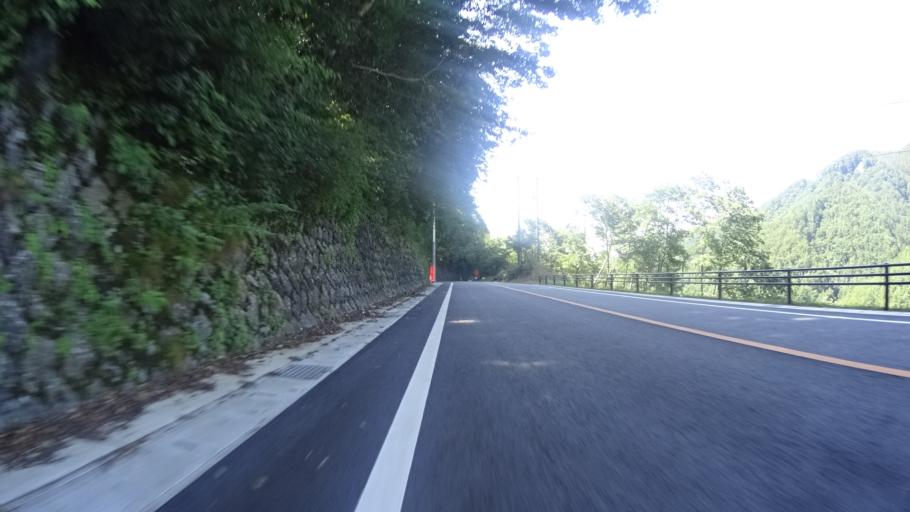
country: JP
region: Yamanashi
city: Enzan
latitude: 35.7735
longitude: 138.8046
